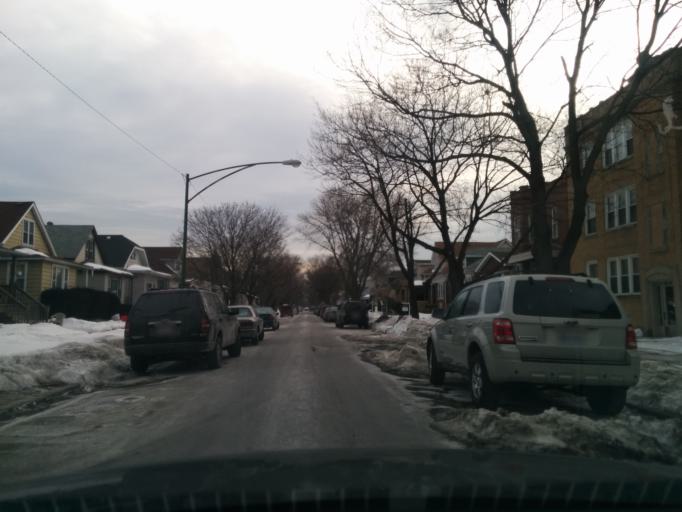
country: US
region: Illinois
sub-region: Cook County
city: Harwood Heights
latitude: 41.9479
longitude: -87.7544
